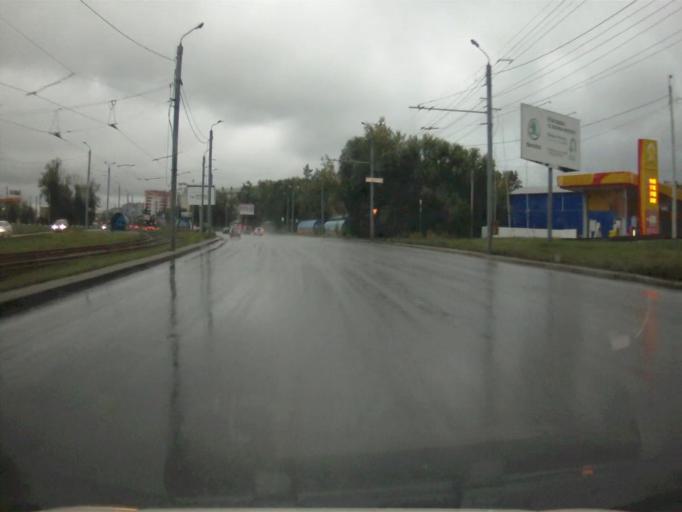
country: RU
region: Chelyabinsk
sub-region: Gorod Chelyabinsk
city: Chelyabinsk
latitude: 55.1501
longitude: 61.4422
